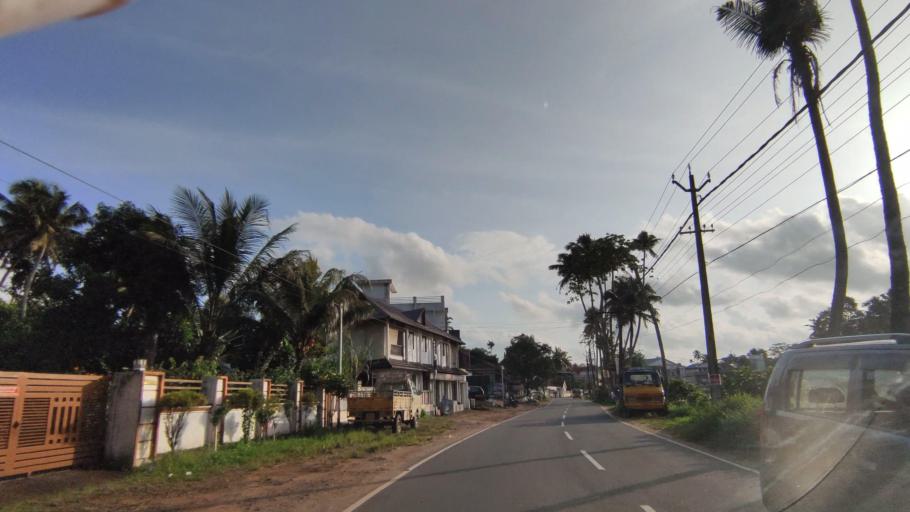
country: IN
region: Kerala
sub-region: Kottayam
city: Kottayam
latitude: 9.5913
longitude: 76.4999
